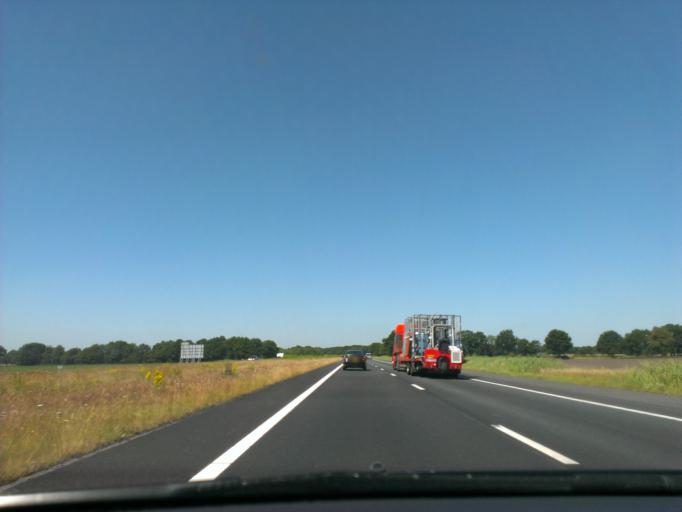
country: NL
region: Drenthe
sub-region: Gemeente Coevorden
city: Dalen
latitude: 52.7235
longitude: 6.7125
